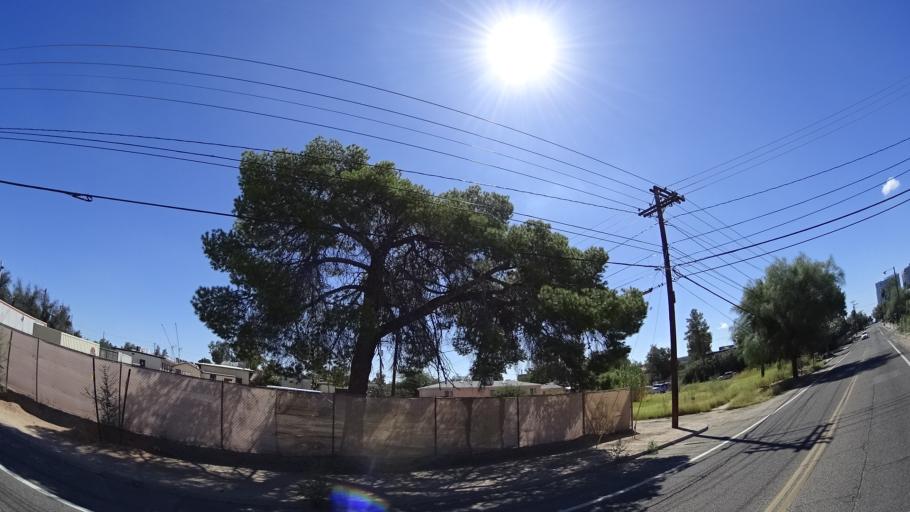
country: US
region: Arizona
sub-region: Pima County
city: Tucson
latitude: 32.2403
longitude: -110.9568
